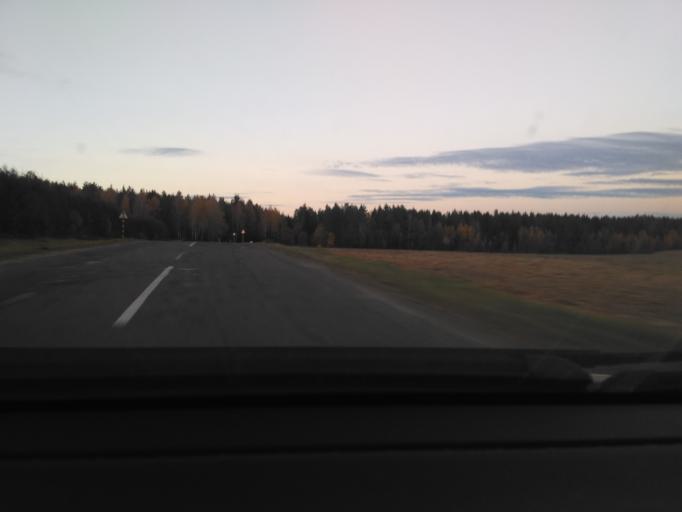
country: BY
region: Minsk
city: Loshnitsa
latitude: 54.3684
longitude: 28.6234
